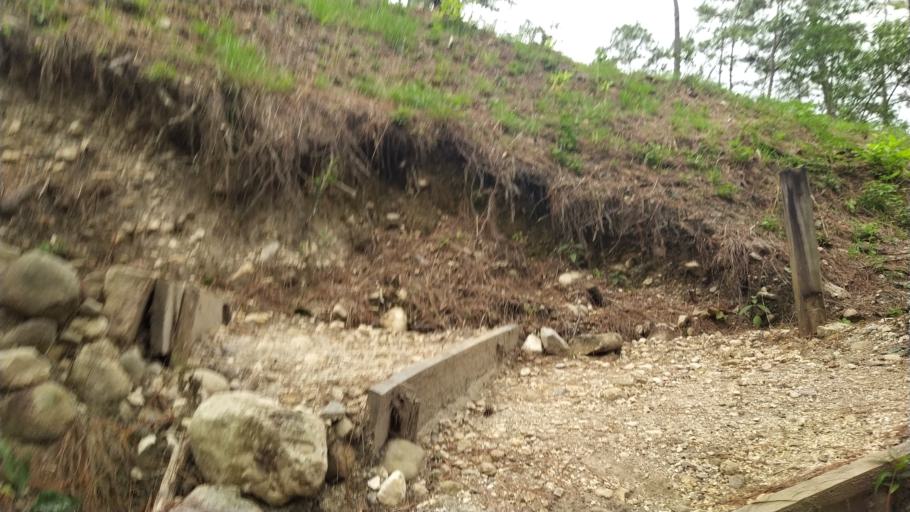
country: GT
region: Chiquimula
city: Esquipulas
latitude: 14.5548
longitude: -89.3191
